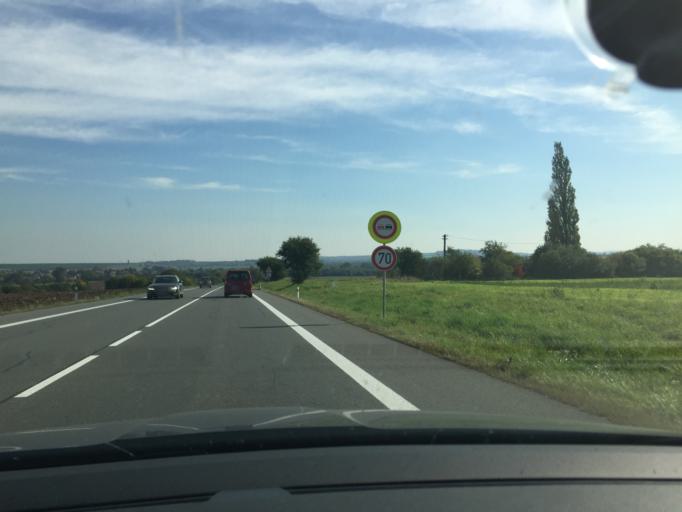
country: CZ
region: Central Bohemia
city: Planany
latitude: 50.0458
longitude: 15.0070
